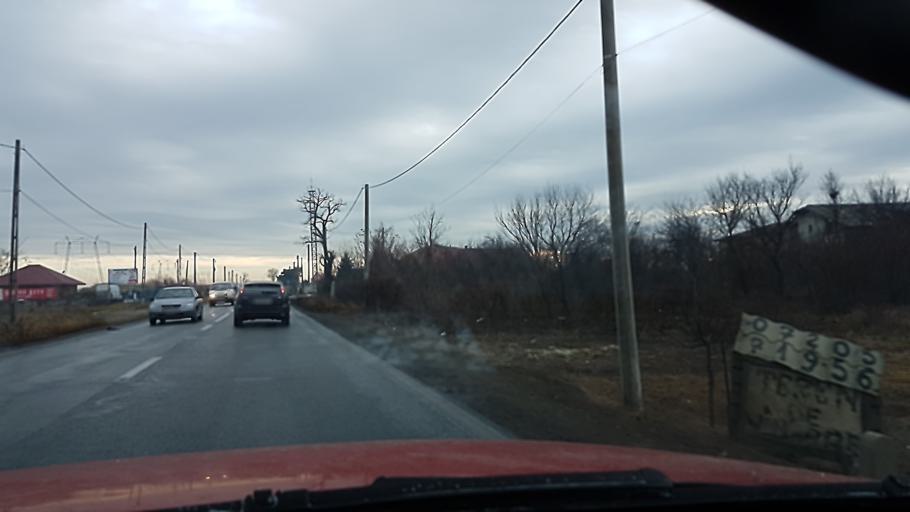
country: RO
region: Calarasi
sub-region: Comuna Frumusani
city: Frumusani
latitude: 44.3168
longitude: 26.2763
